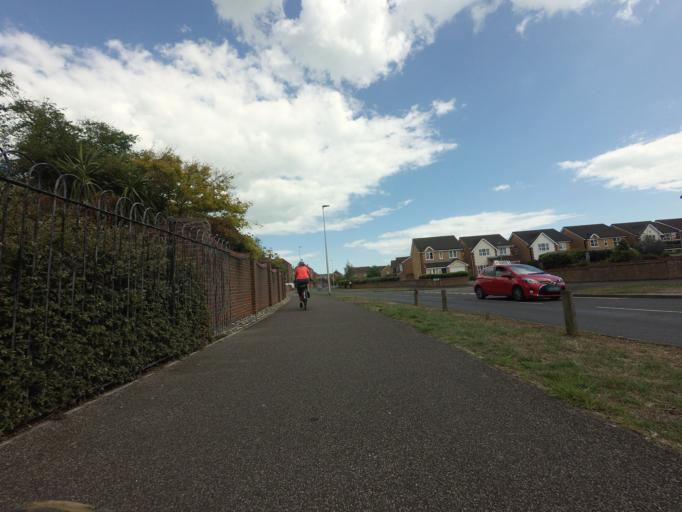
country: GB
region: England
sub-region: East Sussex
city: Pevensey
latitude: 50.7902
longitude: 0.3215
